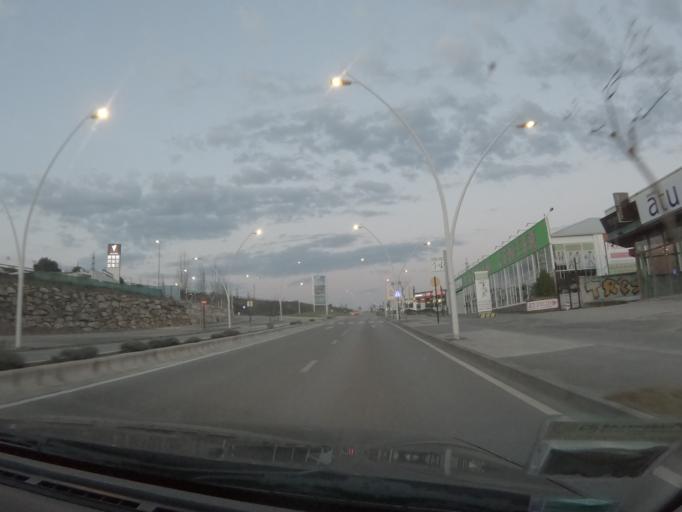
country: ES
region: Castille and Leon
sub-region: Provincia de Leon
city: Ponferrada
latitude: 42.5517
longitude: -6.5731
